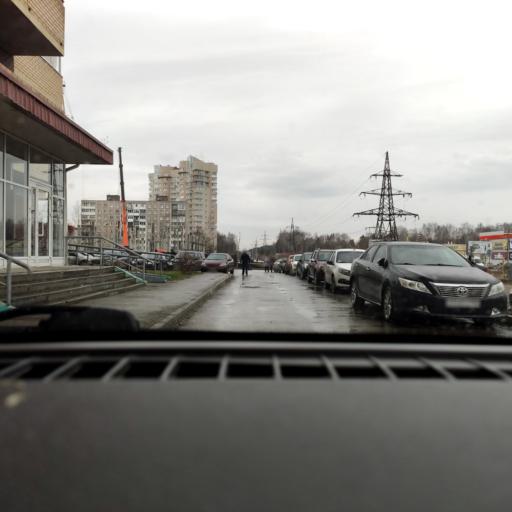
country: RU
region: Perm
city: Kondratovo
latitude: 58.0378
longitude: 56.0284
